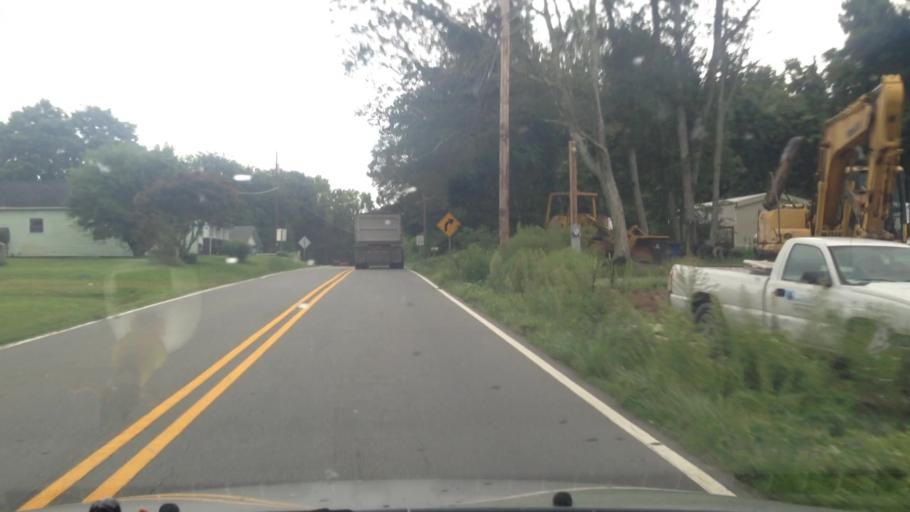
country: US
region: North Carolina
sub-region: Forsyth County
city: Walkertown
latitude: 36.1824
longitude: -80.1547
